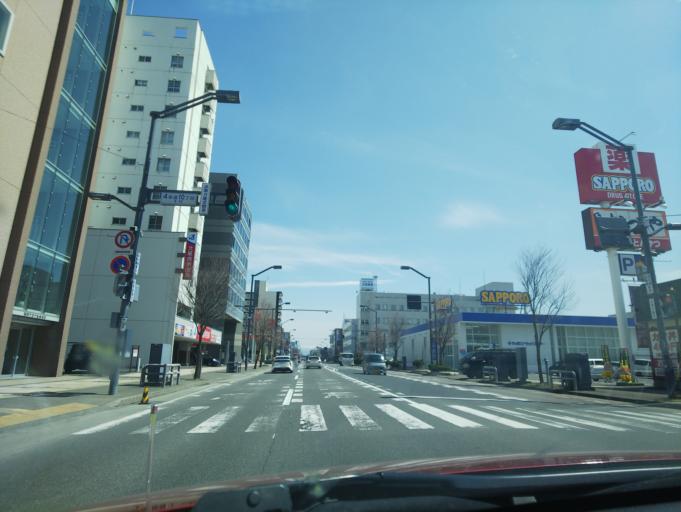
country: JP
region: Hokkaido
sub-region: Asahikawa-shi
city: Asahikawa
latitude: 43.7680
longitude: 142.3642
